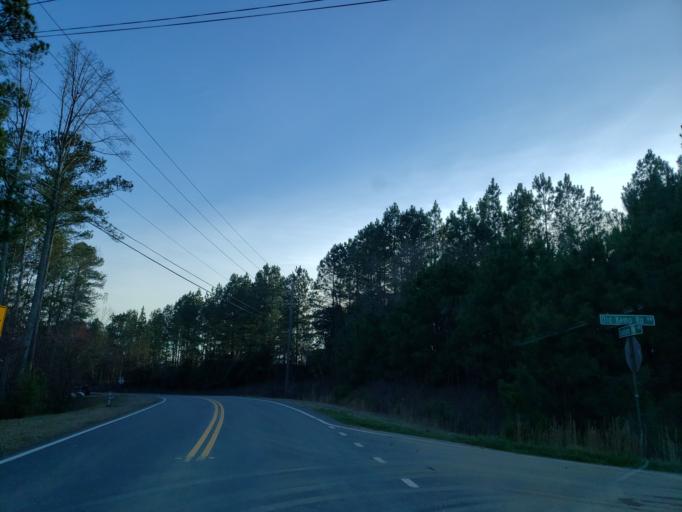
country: US
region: Georgia
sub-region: Cobb County
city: Acworth
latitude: 34.0384
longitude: -84.7285
